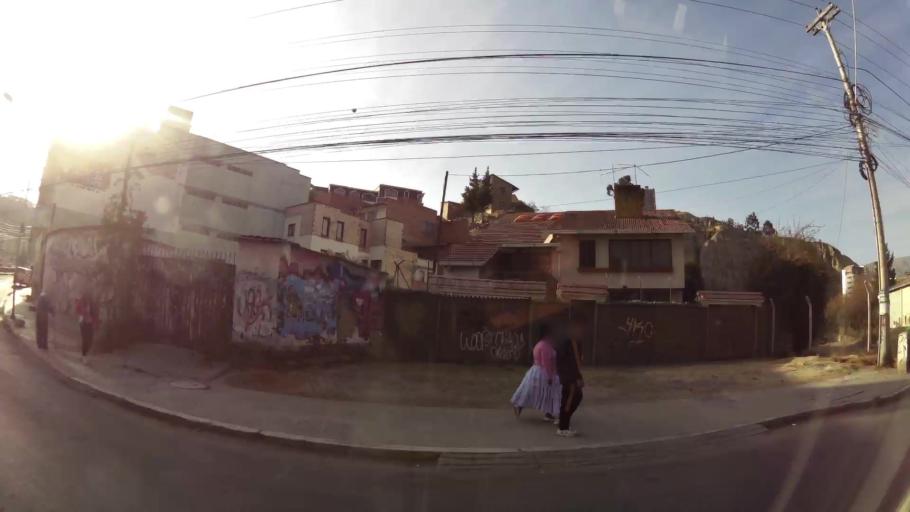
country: BO
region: La Paz
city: La Paz
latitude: -16.5416
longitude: -68.0930
